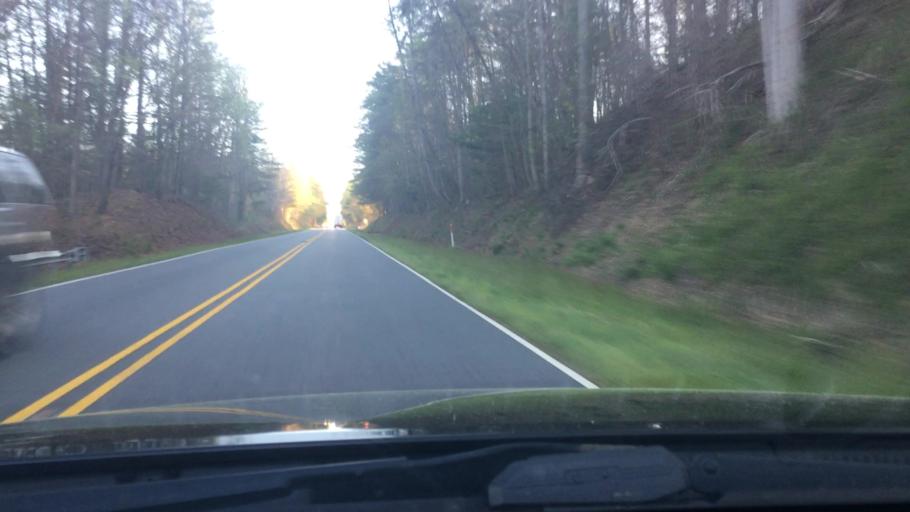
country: US
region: North Carolina
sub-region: Rutherford County
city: Rutherfordton
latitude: 35.4609
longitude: -81.9794
